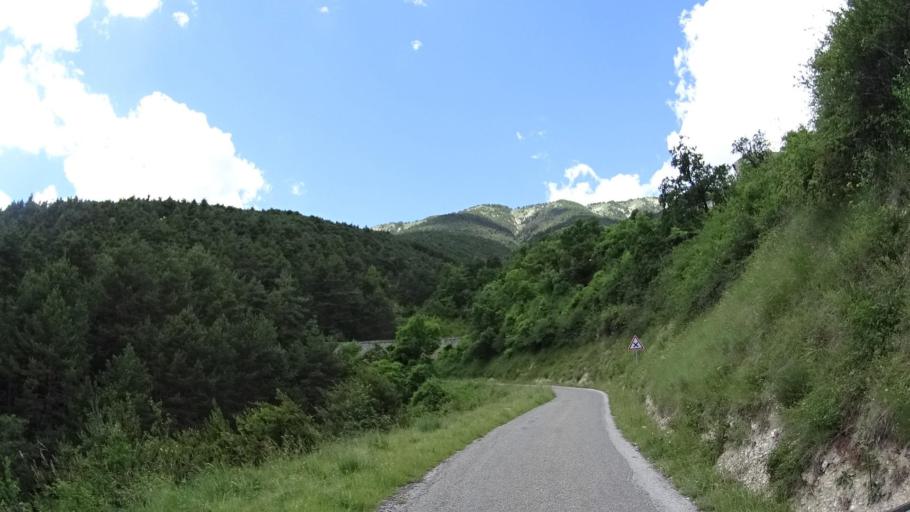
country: FR
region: Provence-Alpes-Cote d'Azur
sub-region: Departement des Alpes-de-Haute-Provence
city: Annot
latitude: 44.0191
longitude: 6.6285
